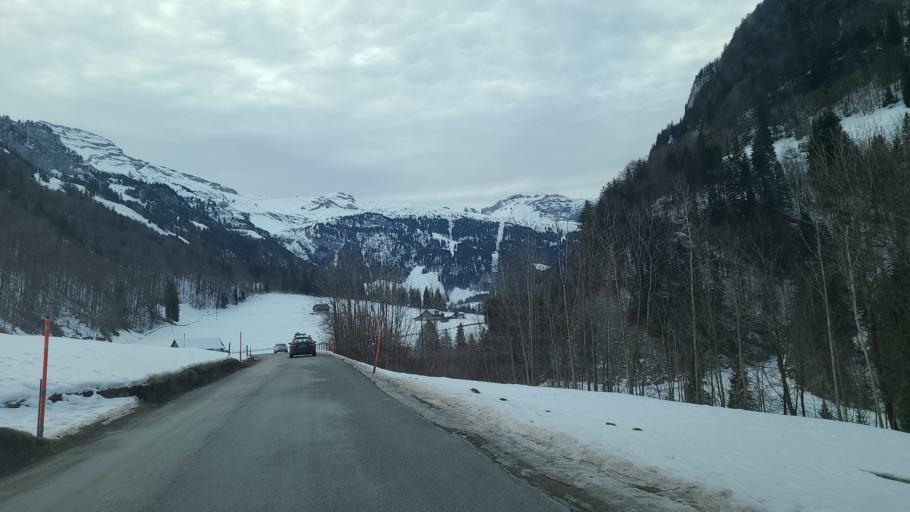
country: CH
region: Obwalden
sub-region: Obwalden
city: Sachseln
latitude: 46.8291
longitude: 8.2868
